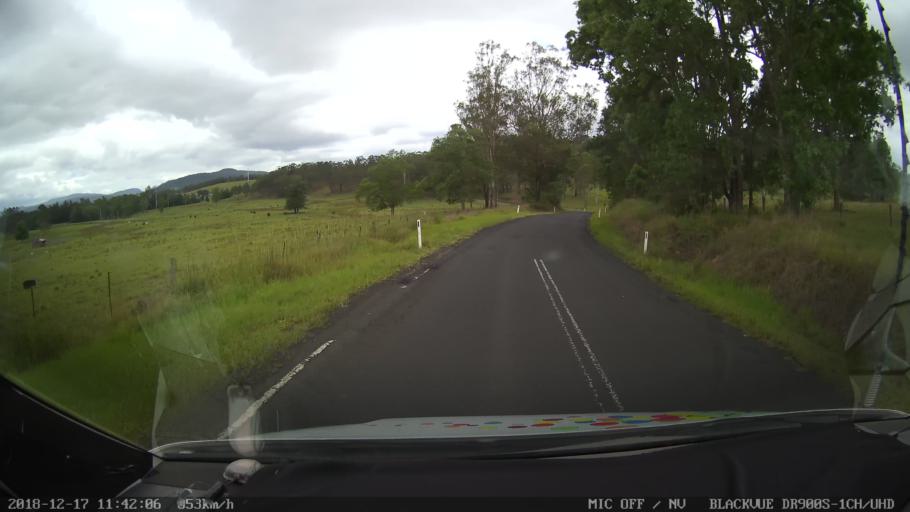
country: AU
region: New South Wales
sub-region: Kyogle
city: Kyogle
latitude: -28.6700
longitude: 152.5885
